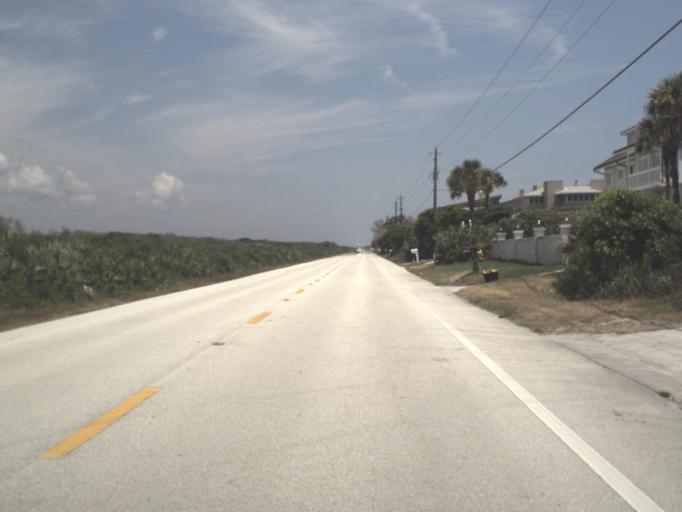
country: US
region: Florida
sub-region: Saint Johns County
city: Villano Beach
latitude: 30.0594
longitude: -81.3321
